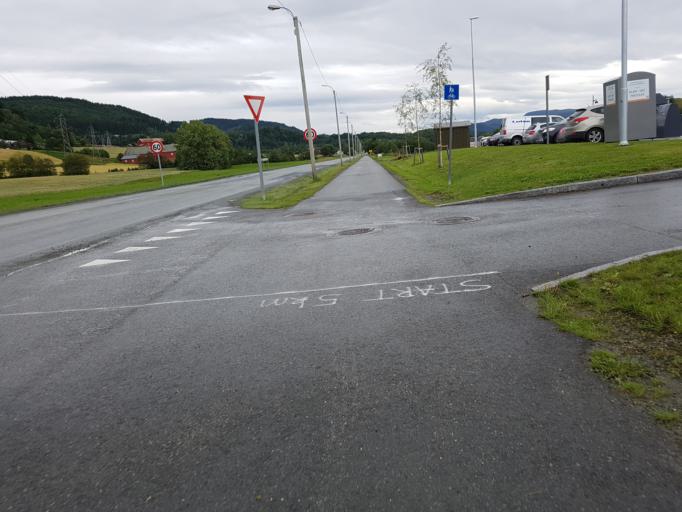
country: NO
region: Sor-Trondelag
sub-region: Trondheim
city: Trondheim
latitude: 63.3871
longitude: 10.4345
